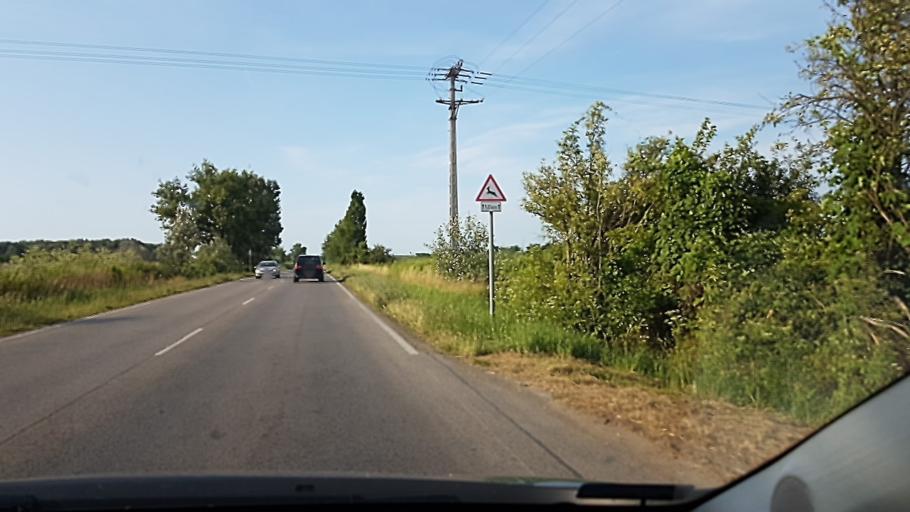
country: HU
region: Pest
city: Dunavarsany
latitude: 47.2996
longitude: 19.0628
